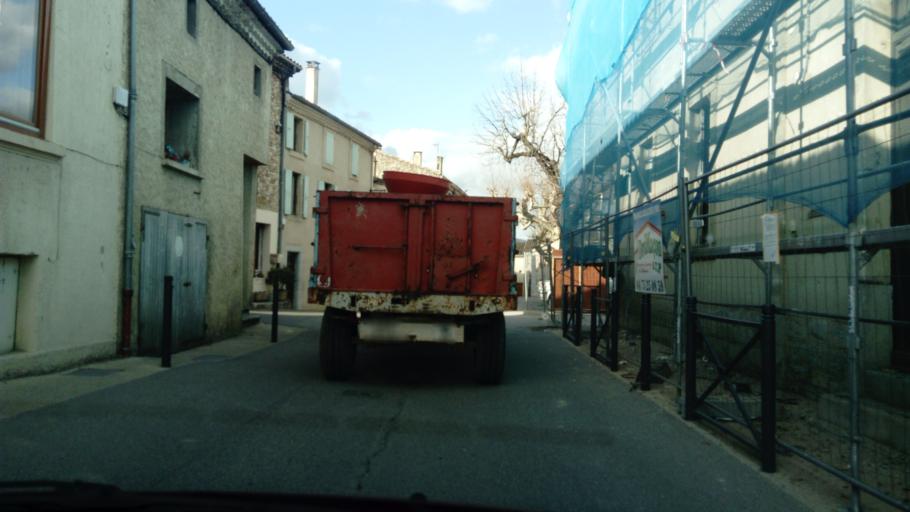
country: FR
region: Rhone-Alpes
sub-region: Departement de la Drome
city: Aouste-sur-Sye
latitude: 44.6987
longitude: 5.0976
